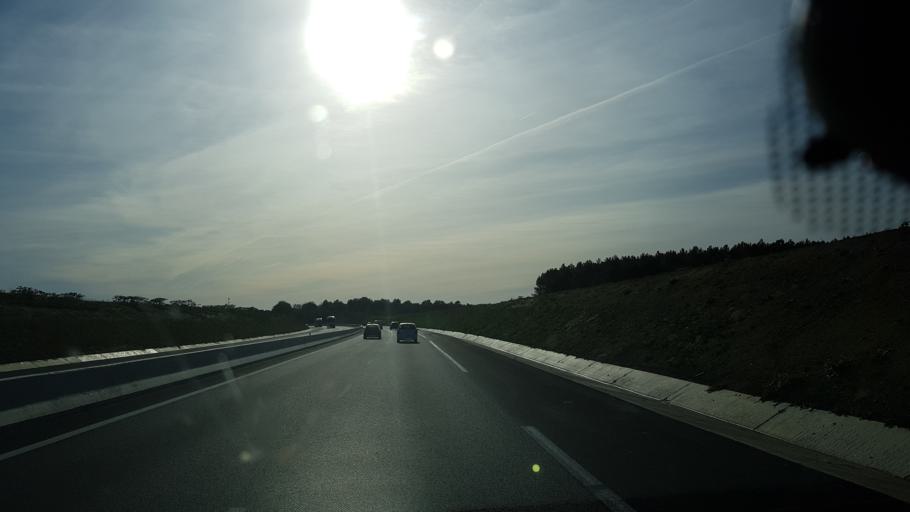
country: FR
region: Poitou-Charentes
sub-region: Departement de la Charente-Maritime
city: Chevanceaux
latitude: 45.3385
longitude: -0.2179
